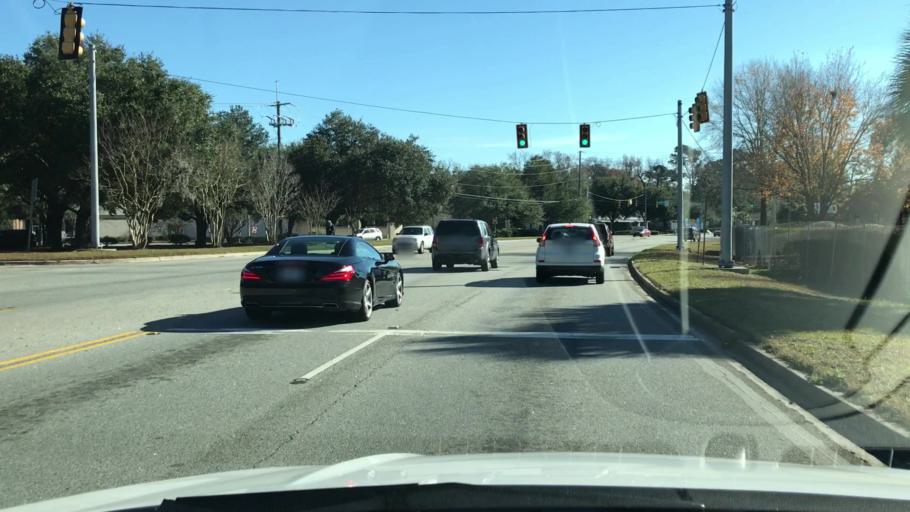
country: US
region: South Carolina
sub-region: Charleston County
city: North Charleston
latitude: 32.8074
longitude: -80.0244
